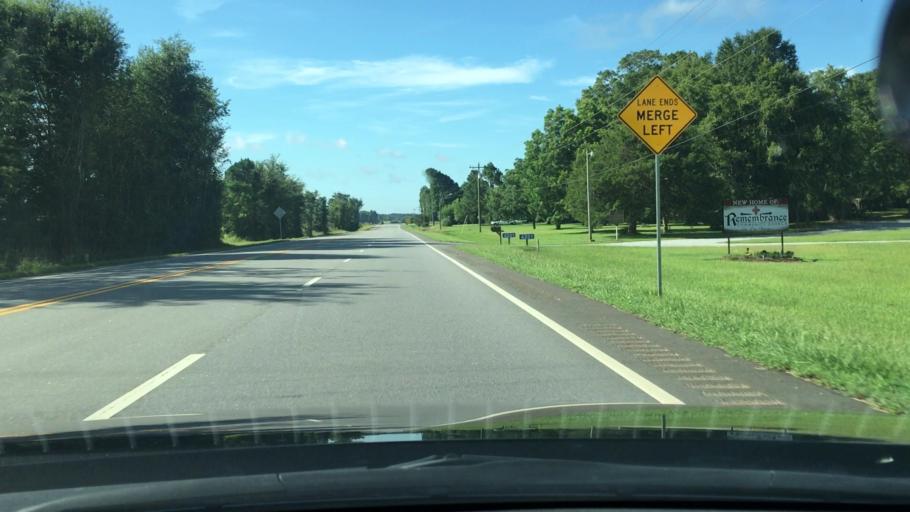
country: US
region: Georgia
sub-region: Morgan County
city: Madison
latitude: 33.4979
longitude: -83.4387
